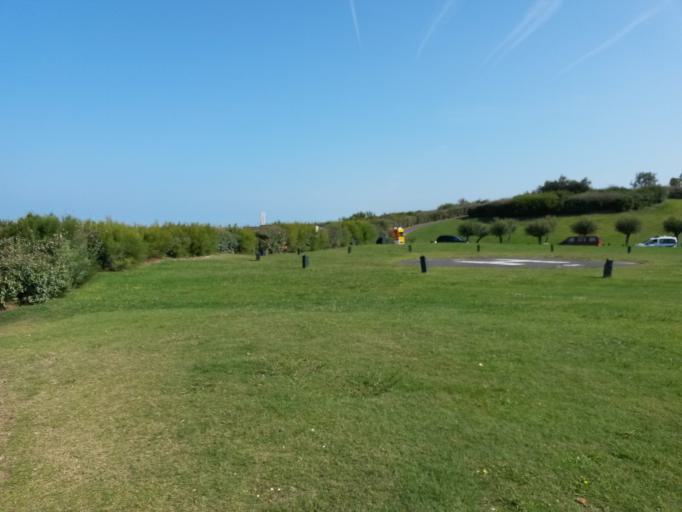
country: FR
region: Aquitaine
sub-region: Departement des Pyrenees-Atlantiques
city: Biarritz
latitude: 43.5055
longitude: -1.5374
